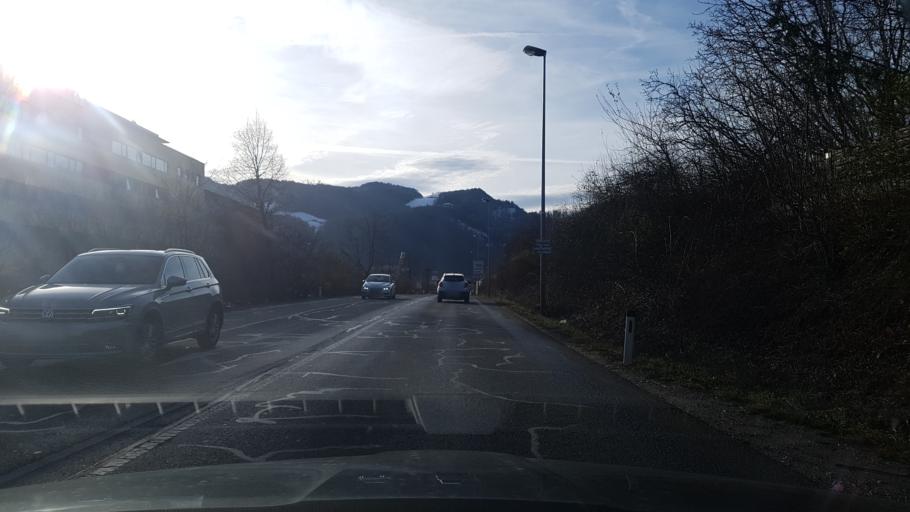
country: AT
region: Salzburg
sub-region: Politischer Bezirk Hallein
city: Hallein
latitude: 47.6866
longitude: 13.1077
